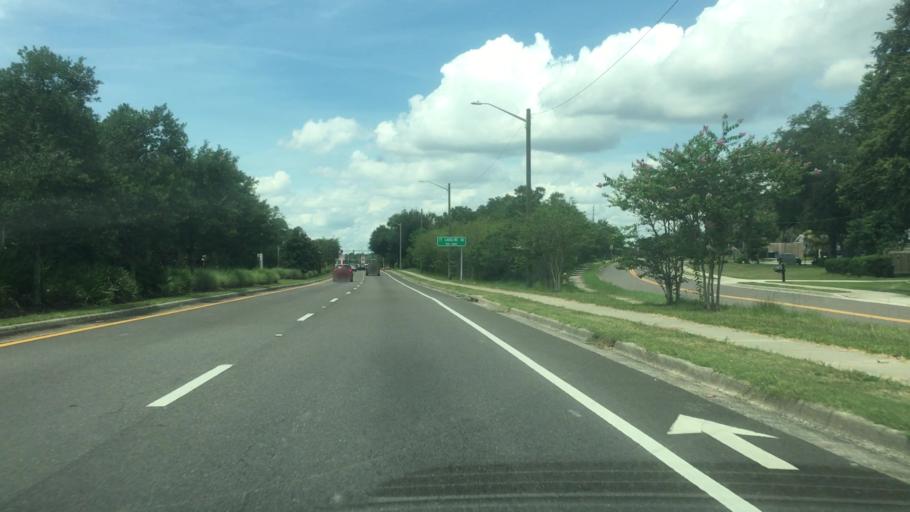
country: US
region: Florida
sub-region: Duval County
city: Jacksonville
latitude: 30.3591
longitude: -81.5516
